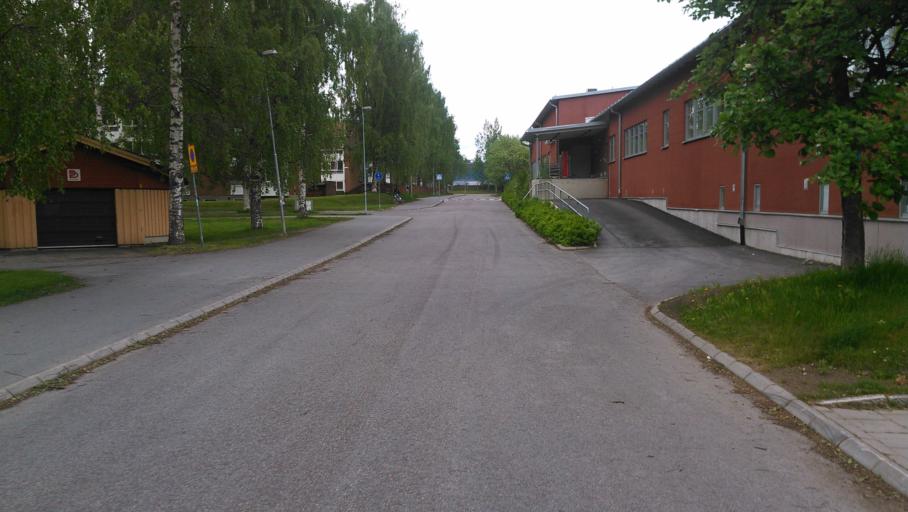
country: SE
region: Vaesterbotten
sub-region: Umea Kommun
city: Umea
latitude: 63.8073
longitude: 20.3151
